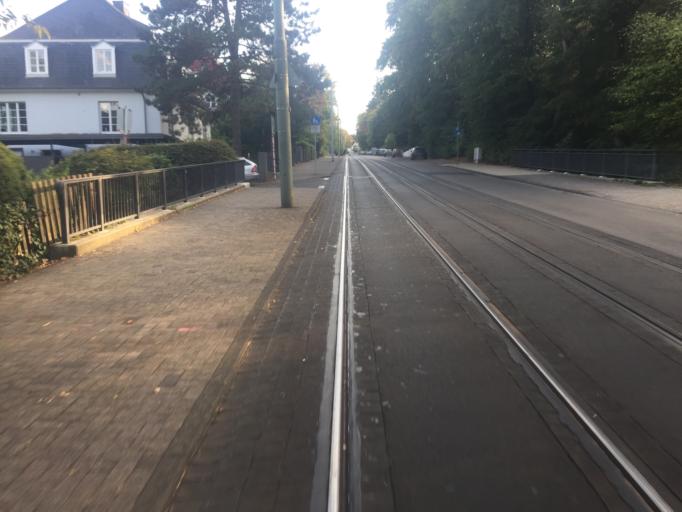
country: DE
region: Hesse
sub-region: Regierungsbezirk Kassel
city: Baunatal
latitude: 51.3059
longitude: 9.4161
